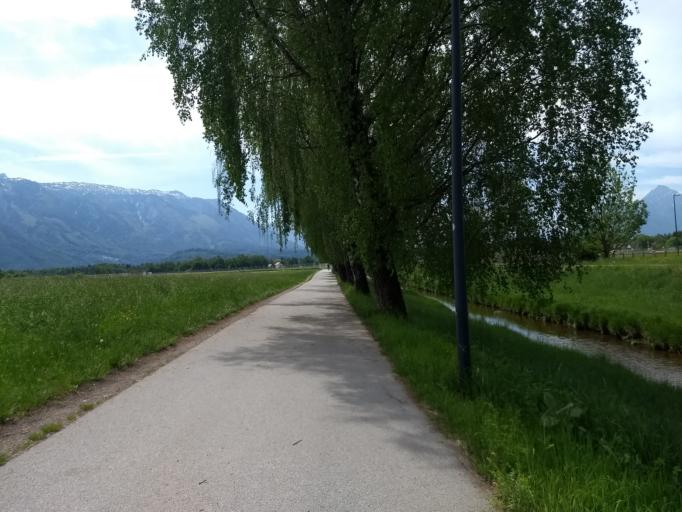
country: AT
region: Salzburg
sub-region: Salzburg Stadt
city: Salzburg
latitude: 47.7827
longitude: 13.0150
